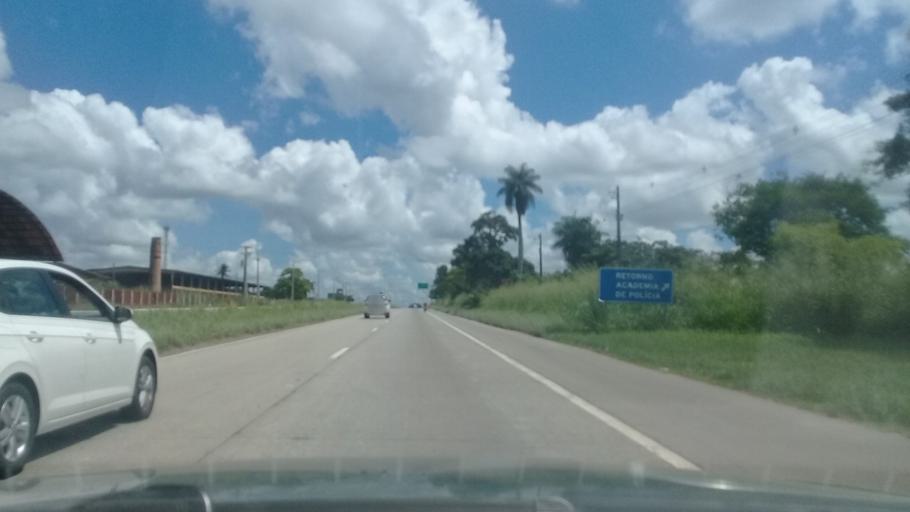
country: BR
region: Pernambuco
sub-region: Carpina
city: Carpina
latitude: -7.9194
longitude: -35.1620
